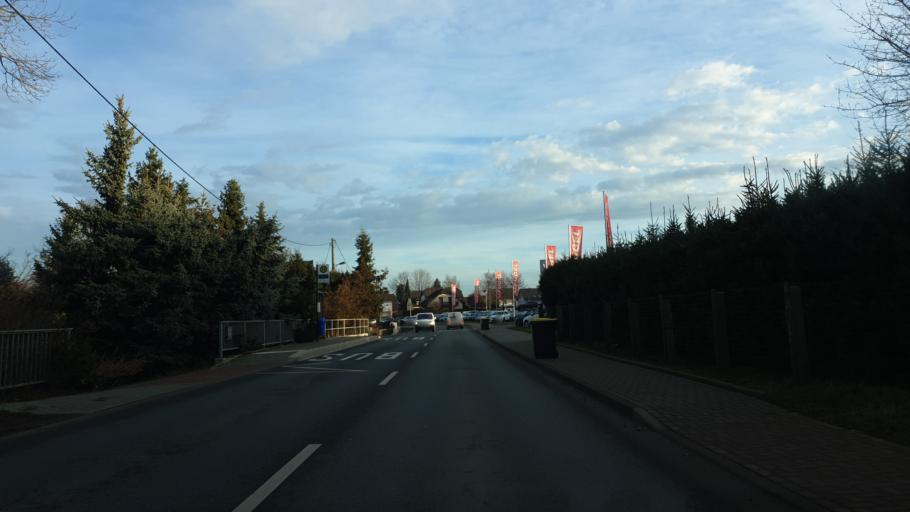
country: DE
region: Saxony
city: Neukirchen
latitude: 50.8021
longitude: 12.8050
